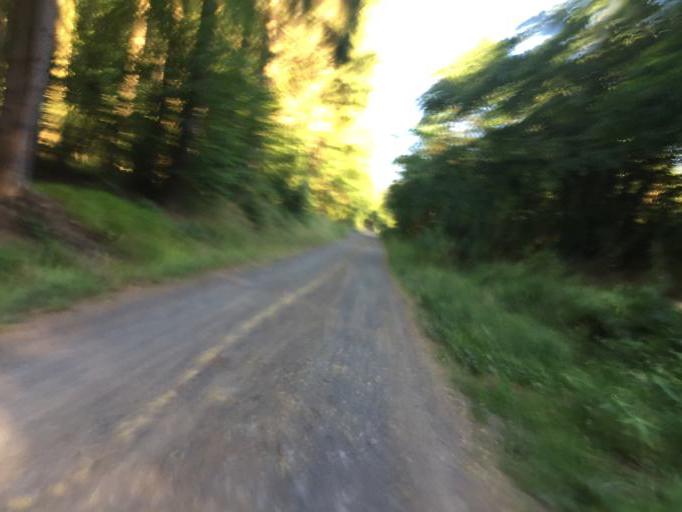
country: DE
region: Rheinland-Pfalz
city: Berod bei Wallmerod
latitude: 50.4931
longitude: 7.9296
